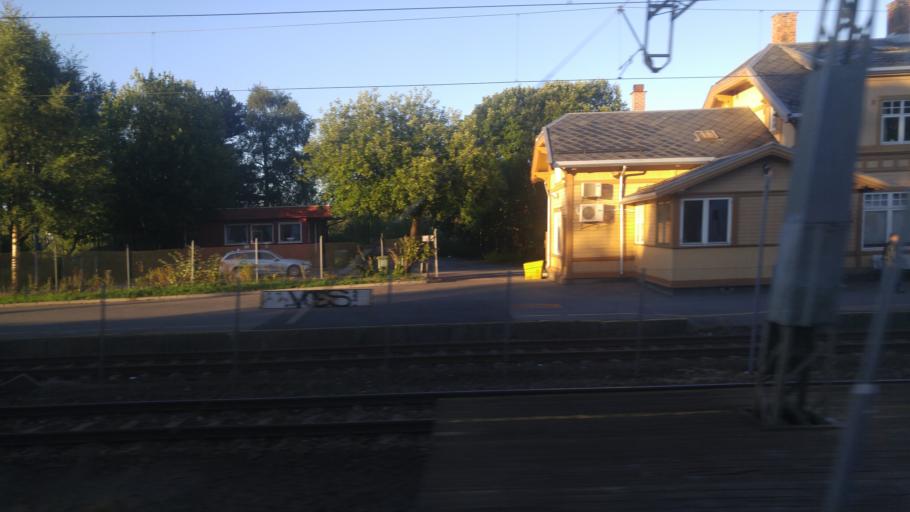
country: NO
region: Akershus
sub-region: Lorenskog
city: Kjenn
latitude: 59.9450
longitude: 10.9457
